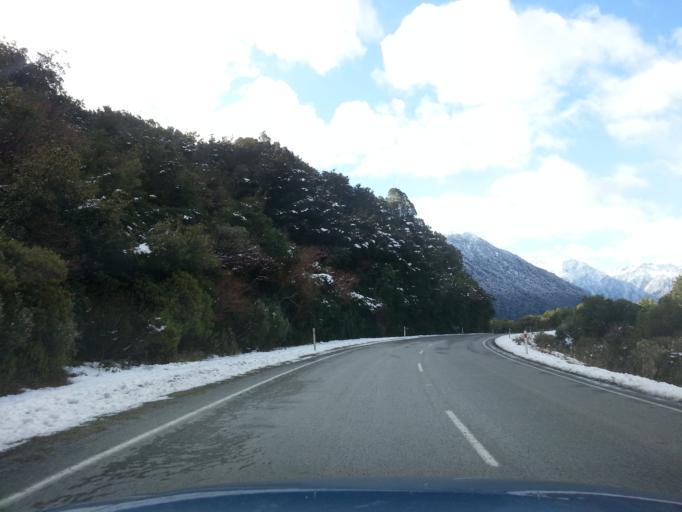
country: NZ
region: West Coast
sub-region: Grey District
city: Greymouth
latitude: -42.8188
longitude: 171.5635
